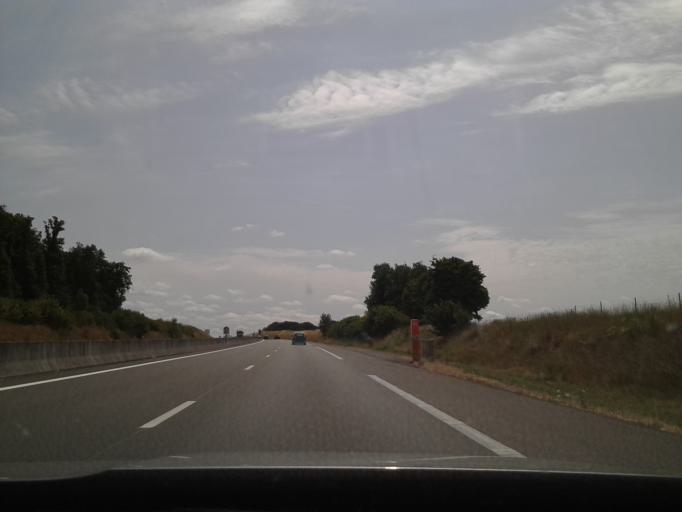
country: FR
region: Centre
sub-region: Departement d'Indre-et-Loire
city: Neuille-Pont-Pierre
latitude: 47.5895
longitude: 0.5534
